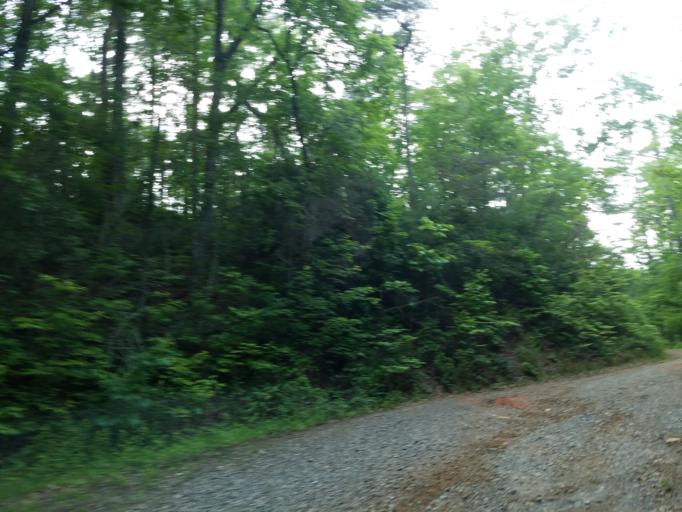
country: US
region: Georgia
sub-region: Dawson County
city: Dawsonville
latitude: 34.5732
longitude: -84.1408
